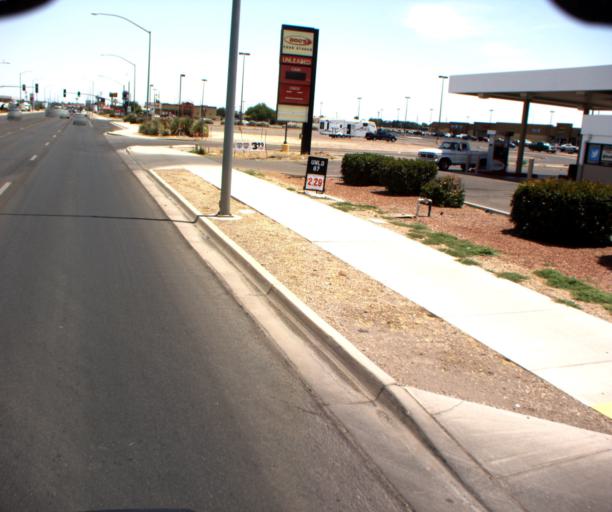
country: US
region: Arizona
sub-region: Graham County
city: Thatcher
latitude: 32.8409
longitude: -109.7392
